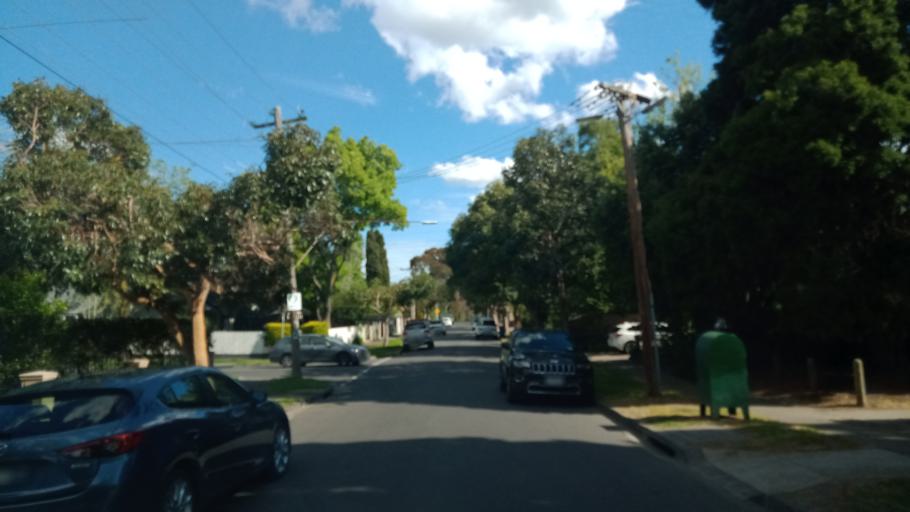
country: AU
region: Victoria
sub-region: Stonnington
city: Glen Iris
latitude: -37.8509
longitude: 145.0559
